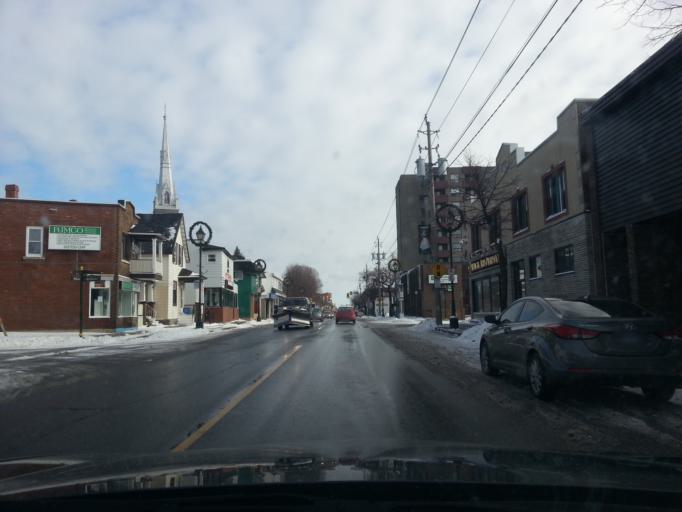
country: CA
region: Ontario
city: Cornwall
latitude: 45.0185
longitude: -74.7137
